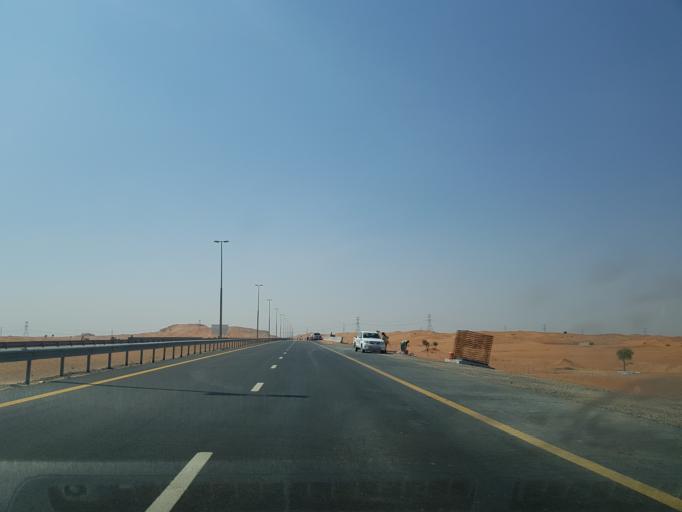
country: AE
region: Ash Shariqah
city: Adh Dhayd
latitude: 25.2442
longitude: 55.8608
